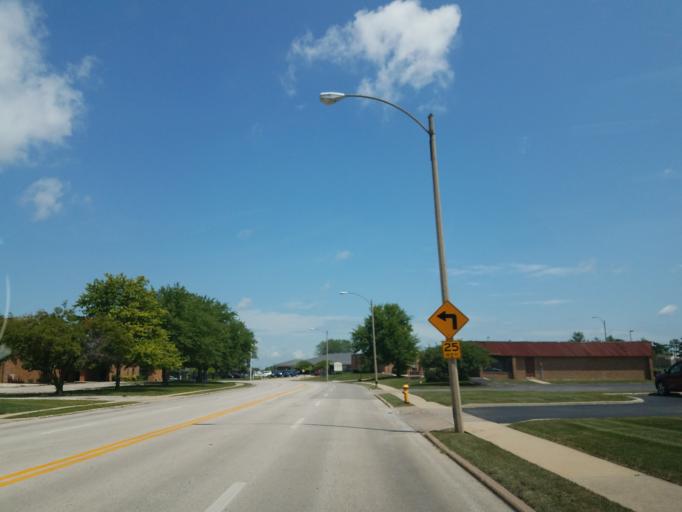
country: US
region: Illinois
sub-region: McLean County
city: Bloomington
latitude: 40.4808
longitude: -88.9593
